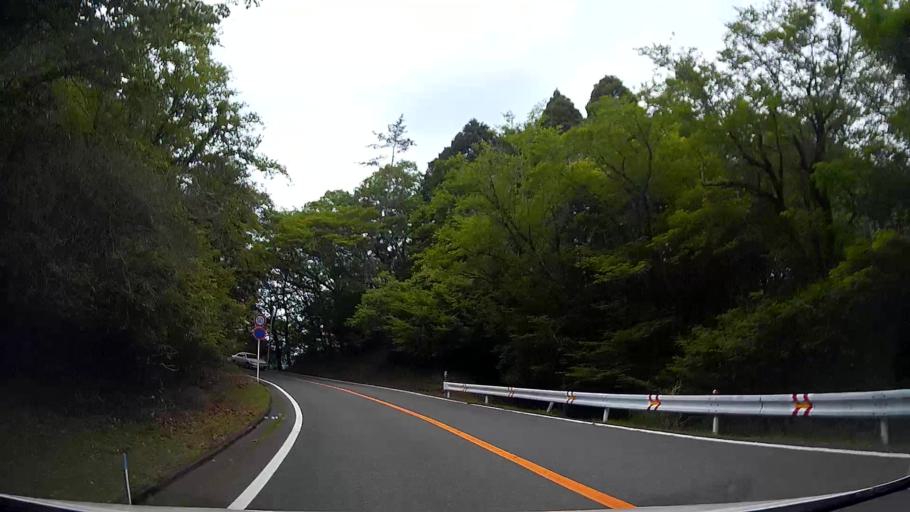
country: JP
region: Shizuoka
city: Ito
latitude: 34.9072
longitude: 139.0715
